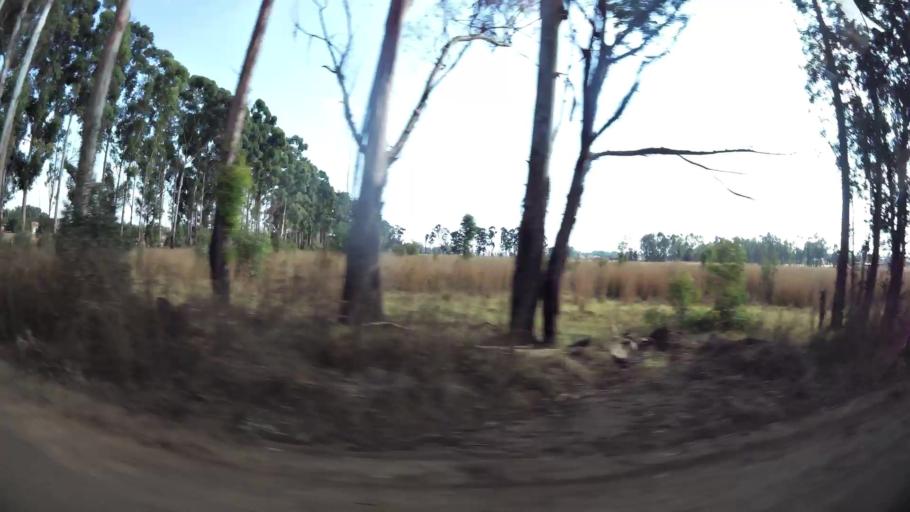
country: ZA
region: Gauteng
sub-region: Ekurhuleni Metropolitan Municipality
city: Benoni
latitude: -26.0857
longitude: 28.3678
